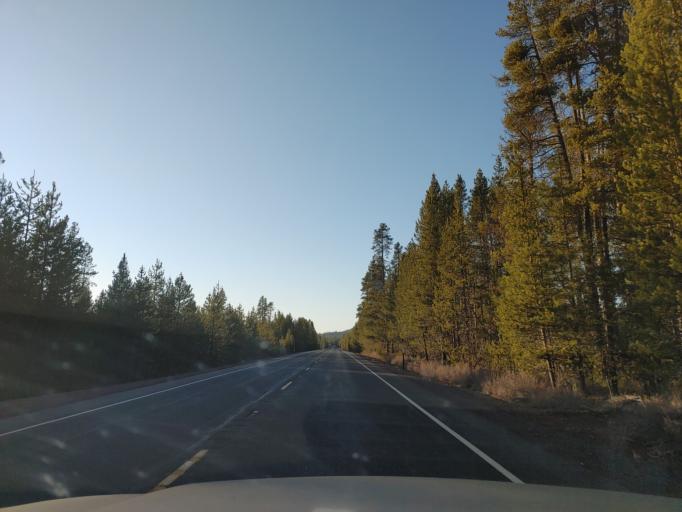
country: US
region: Oregon
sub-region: Deschutes County
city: La Pine
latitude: 43.4133
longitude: -121.8338
